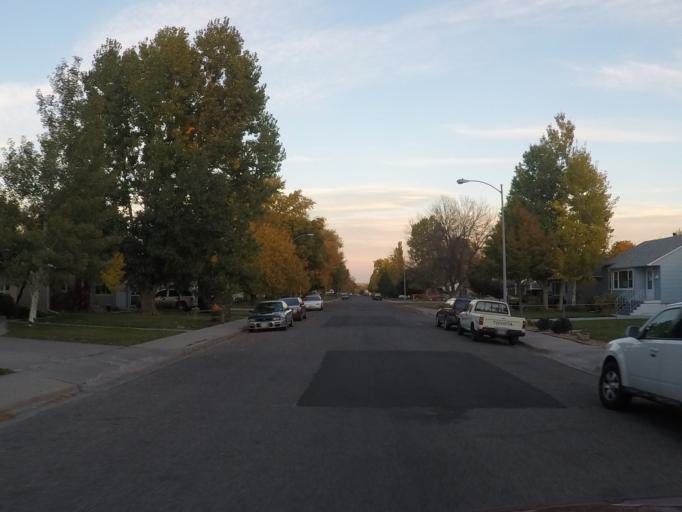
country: US
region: Montana
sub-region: Yellowstone County
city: Billings
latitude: 45.7879
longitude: -108.5448
